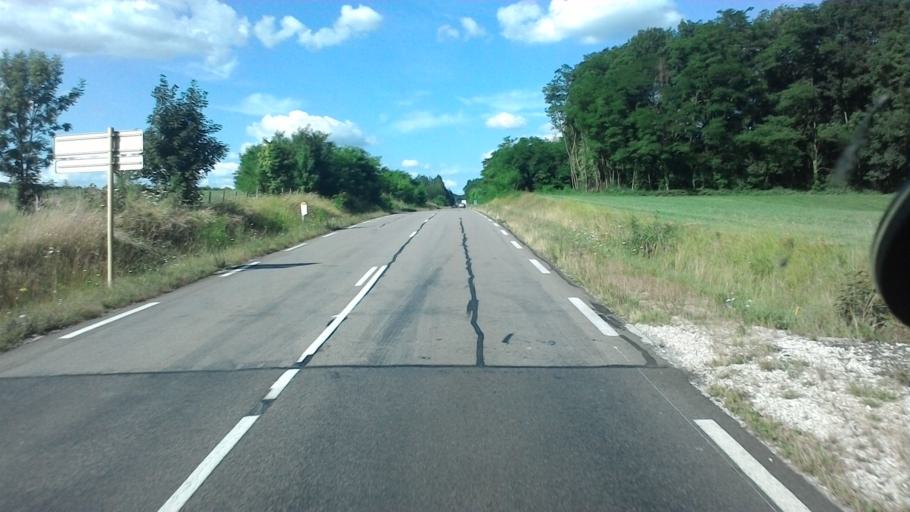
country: FR
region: Franche-Comte
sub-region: Departement de la Haute-Saone
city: Rioz
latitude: 47.5180
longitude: 6.0033
